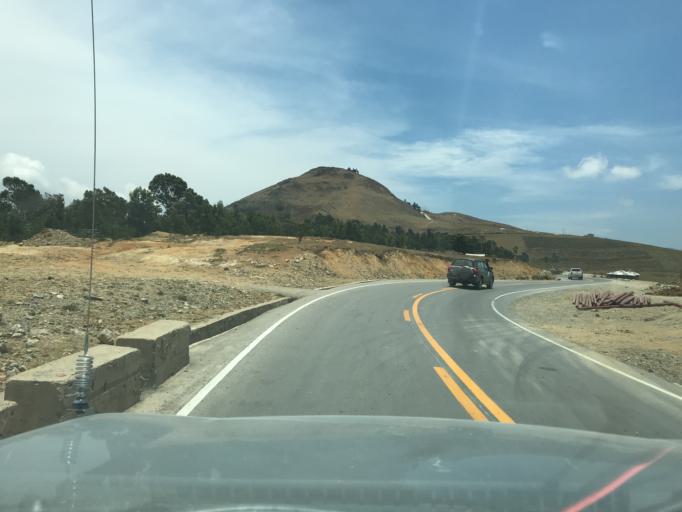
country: TL
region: Manufahi
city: Same
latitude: -8.8776
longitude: 125.6004
